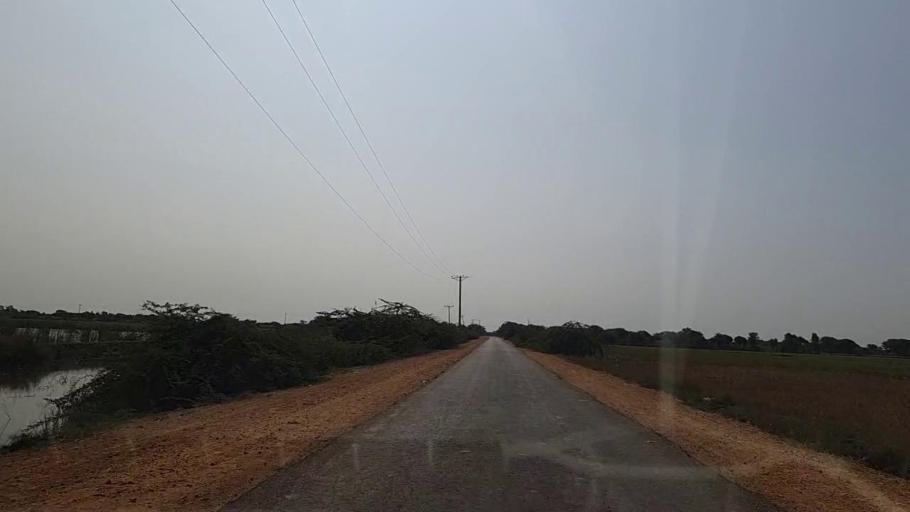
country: PK
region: Sindh
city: Chuhar Jamali
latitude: 24.3271
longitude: 67.9432
